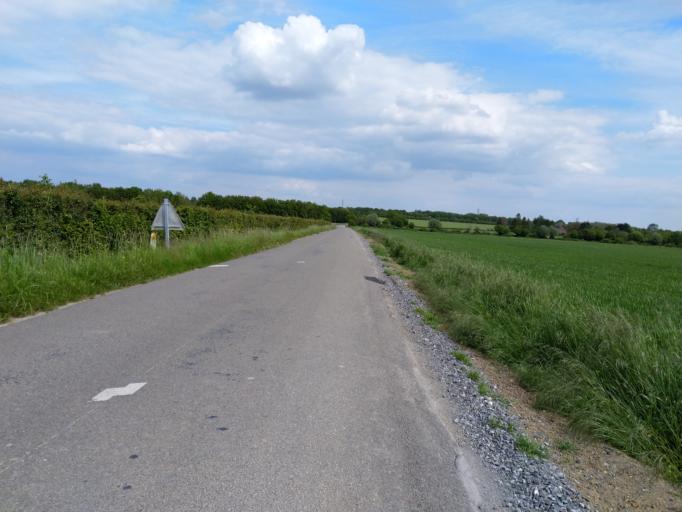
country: FR
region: Picardie
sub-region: Departement de l'Aisne
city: Boue
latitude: 50.0253
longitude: 3.6806
